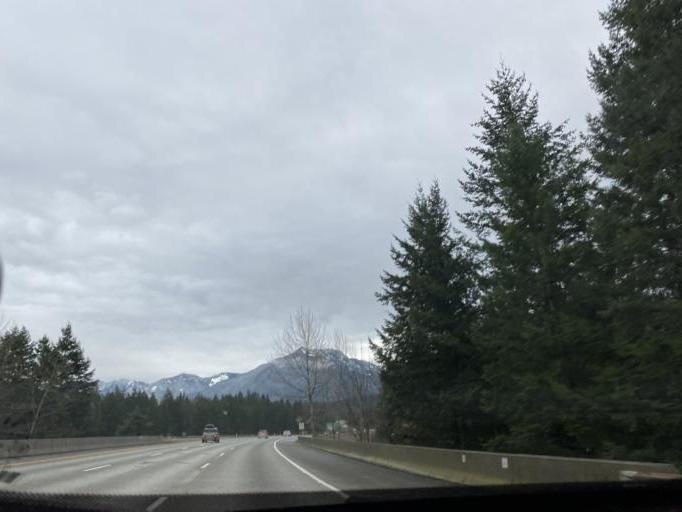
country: US
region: Washington
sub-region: King County
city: Tanner
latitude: 47.4731
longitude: -121.7443
